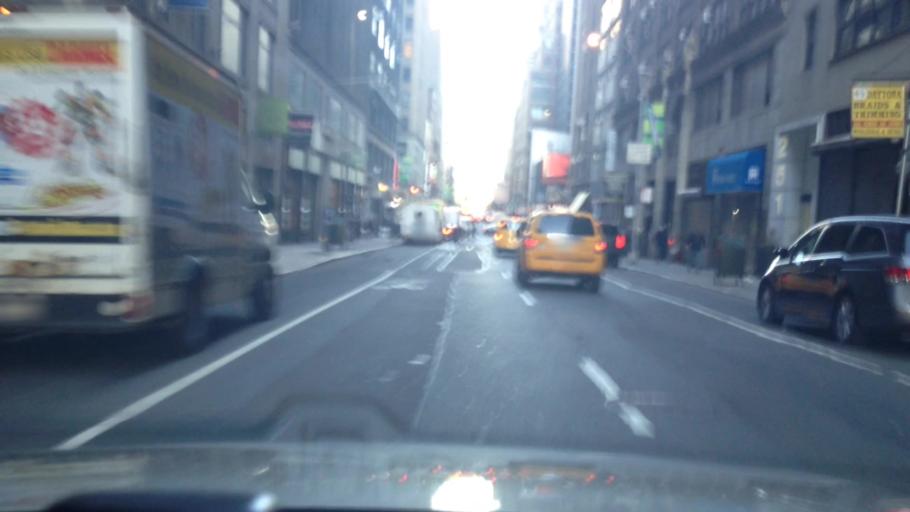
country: US
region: New Jersey
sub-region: Hudson County
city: Weehawken
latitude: 40.7549
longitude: -73.9900
